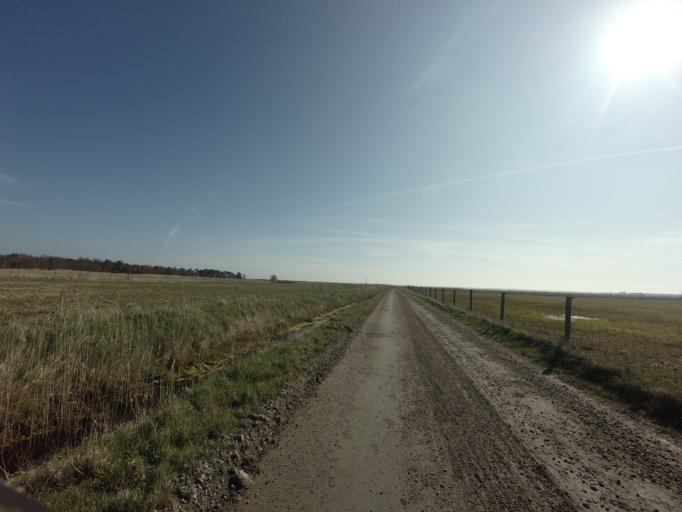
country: SE
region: Skane
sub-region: Vellinge Kommun
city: Skanor med Falsterbo
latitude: 55.4303
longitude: 12.8574
